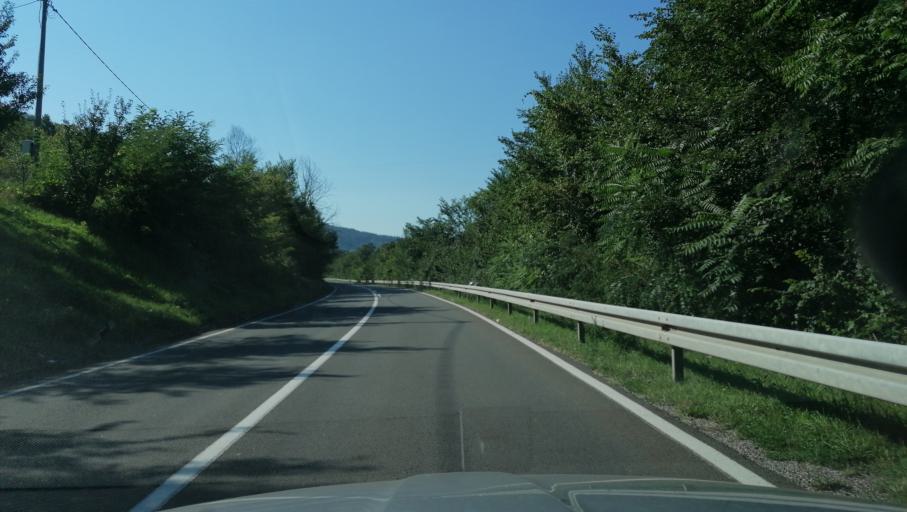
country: RS
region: Central Serbia
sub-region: Raski Okrug
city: Kraljevo
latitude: 43.6660
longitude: 20.5901
